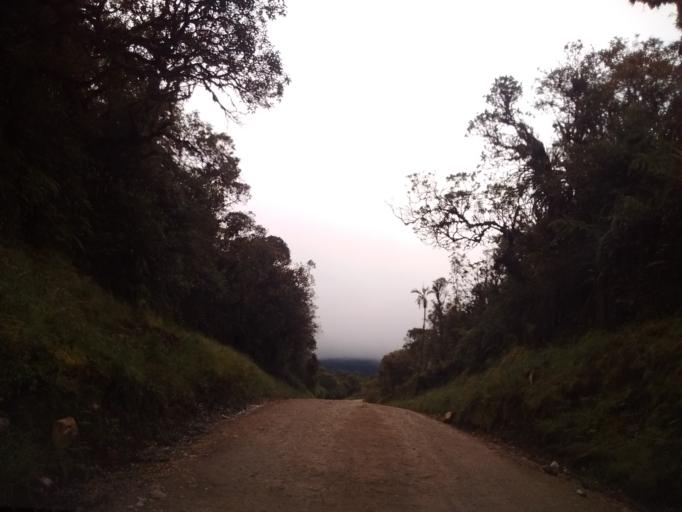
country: CO
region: Huila
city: Isnos
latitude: 2.1216
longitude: -76.3765
